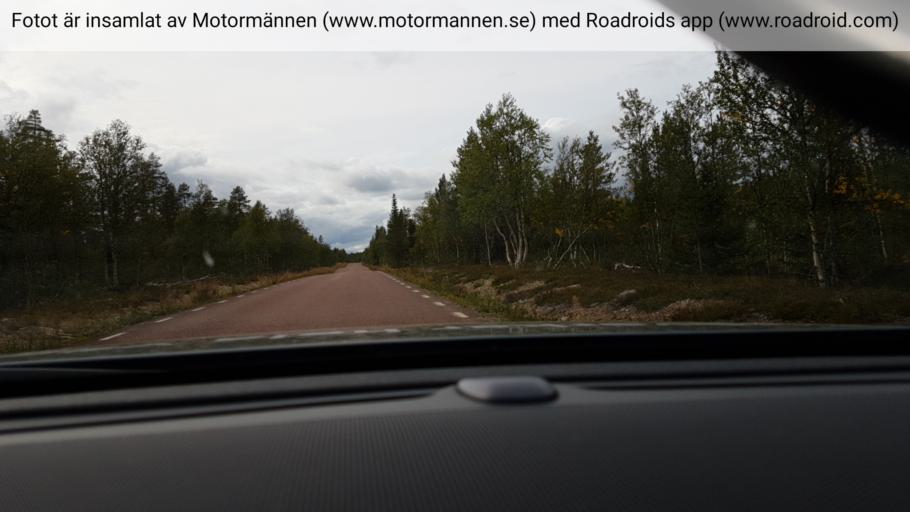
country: NO
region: Hedmark
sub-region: Trysil
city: Innbygda
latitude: 61.6870
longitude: 12.5631
